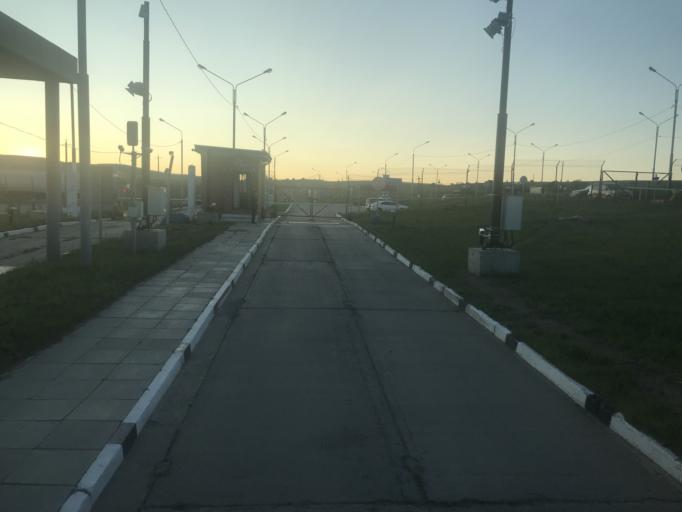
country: MN
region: Selenge
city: Altanbulag
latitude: 50.3270
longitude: 106.4855
